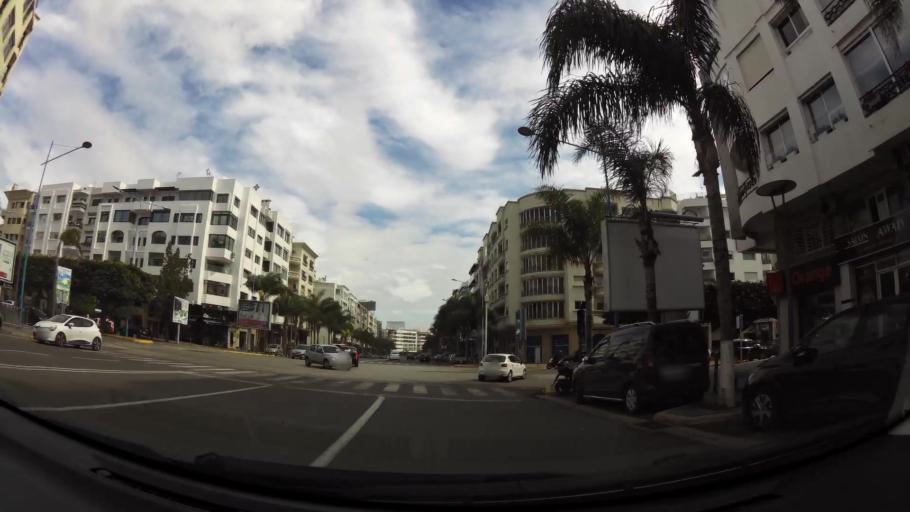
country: MA
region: Grand Casablanca
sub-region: Casablanca
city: Casablanca
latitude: 33.5853
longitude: -7.6455
